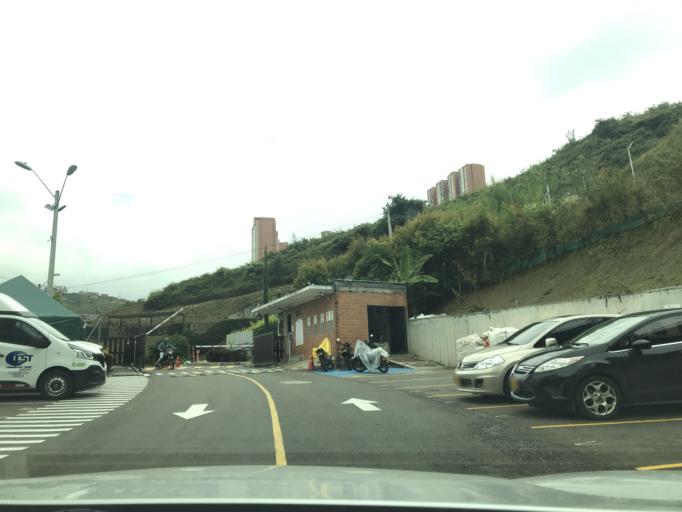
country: CO
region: Antioquia
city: Medellin
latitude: 6.2702
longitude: -75.6053
